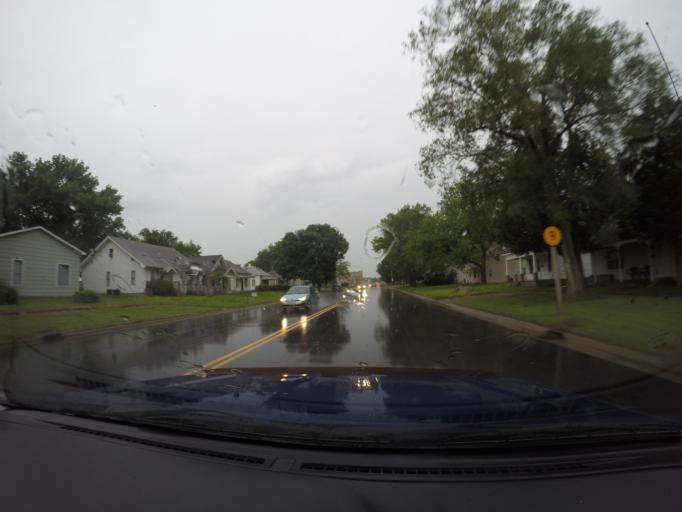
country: US
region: Kansas
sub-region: Cloud County
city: Concordia
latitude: 39.5716
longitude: -97.6542
